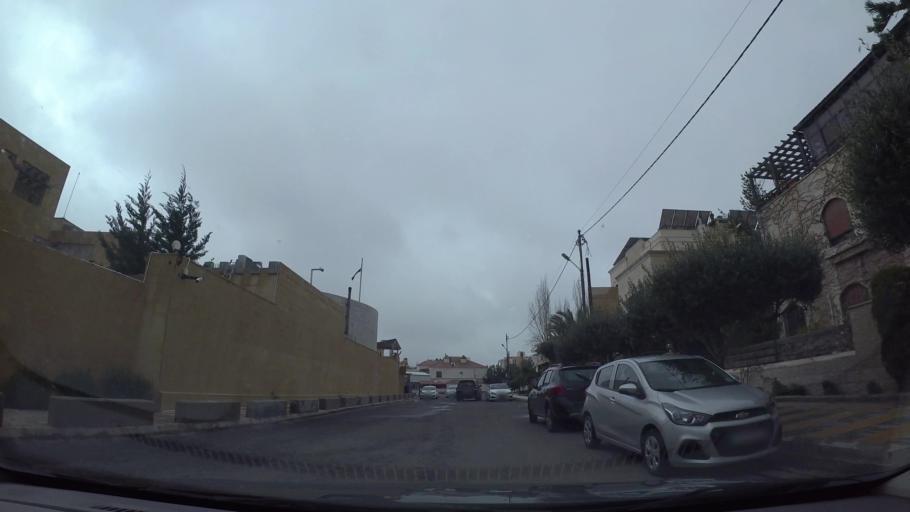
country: JO
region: Amman
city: Al Bunayyat ash Shamaliyah
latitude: 31.9455
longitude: 35.8828
